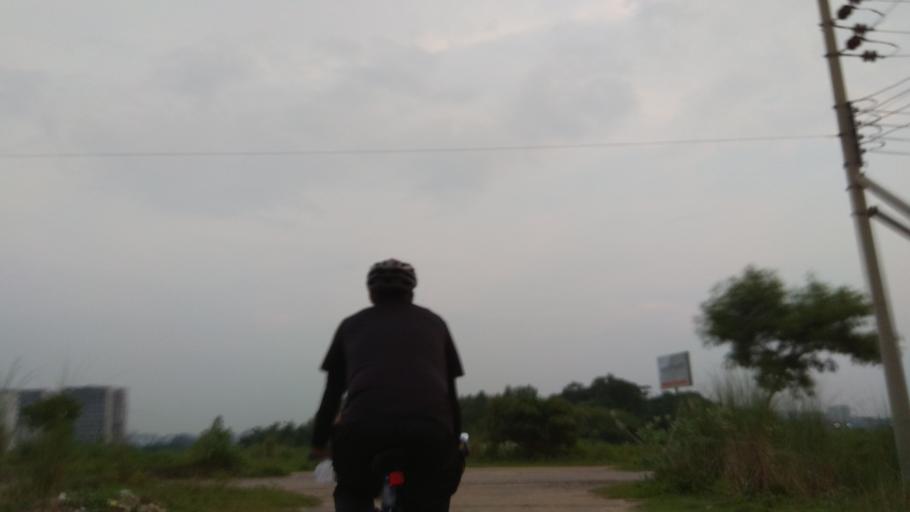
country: BD
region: Dhaka
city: Tungi
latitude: 23.8538
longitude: 90.3684
